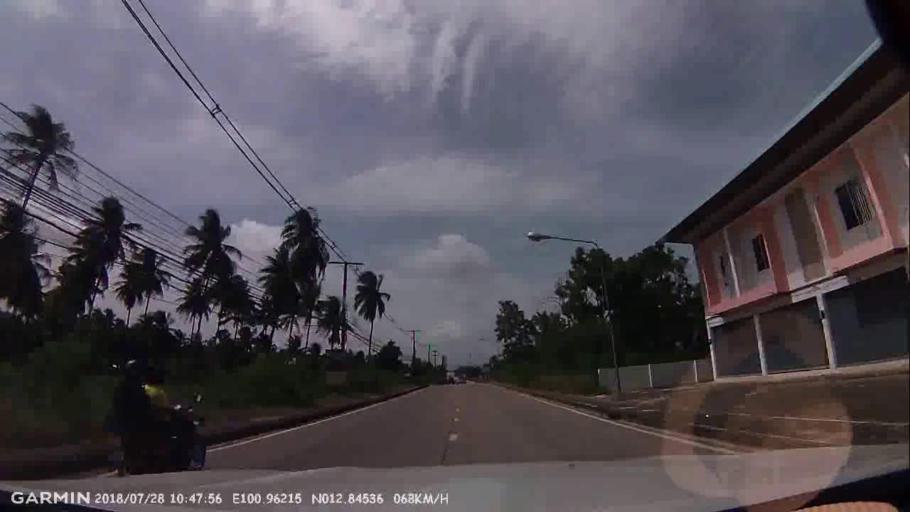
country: TH
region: Chon Buri
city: Phatthaya
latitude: 12.8453
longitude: 100.9622
